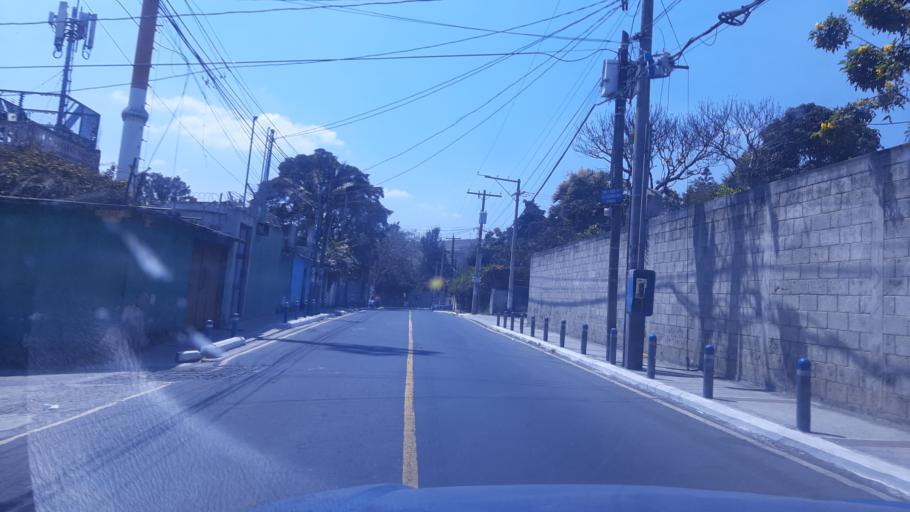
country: GT
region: Guatemala
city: Villa Nueva
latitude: 14.5221
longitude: -90.5930
